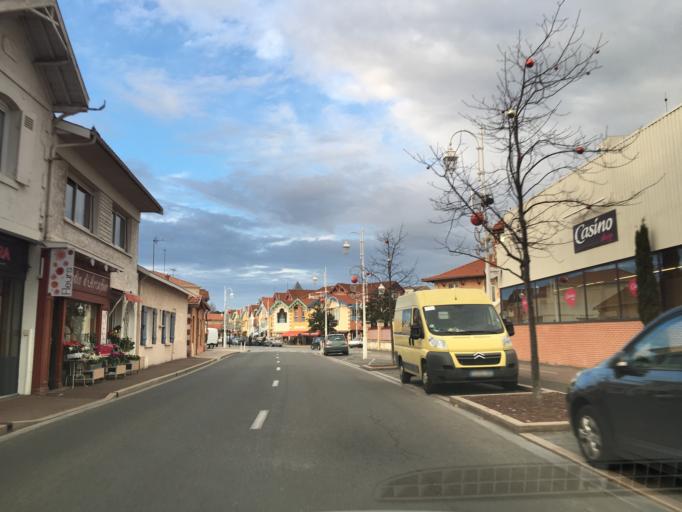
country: FR
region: Aquitaine
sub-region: Departement de la Gironde
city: Arcachon
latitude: 44.6557
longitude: -1.1468
